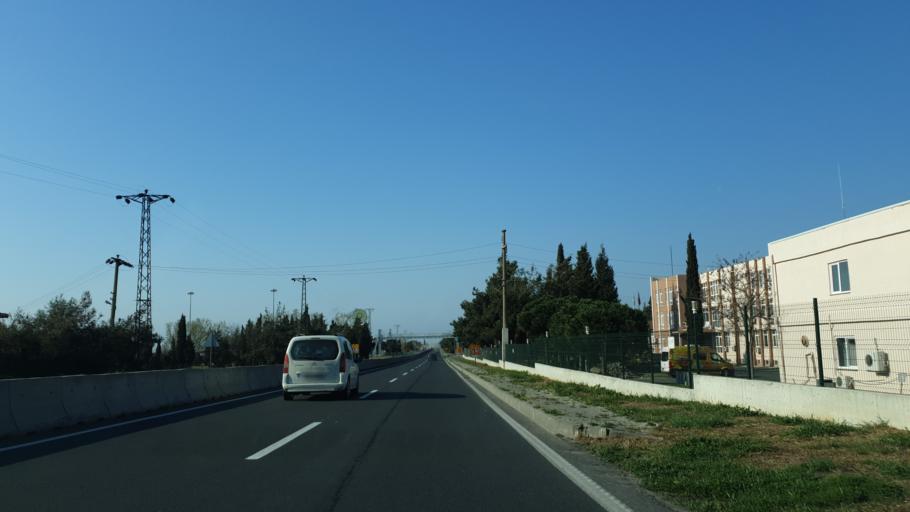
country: TR
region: Tekirdag
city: Corlu
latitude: 41.0219
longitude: 27.7226
